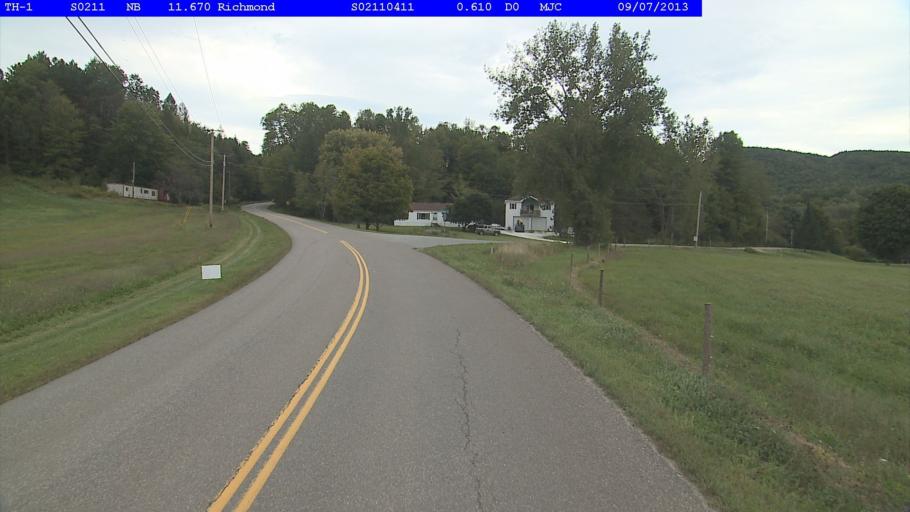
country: US
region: Vermont
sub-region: Chittenden County
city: Williston
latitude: 44.3620
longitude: -72.9937
